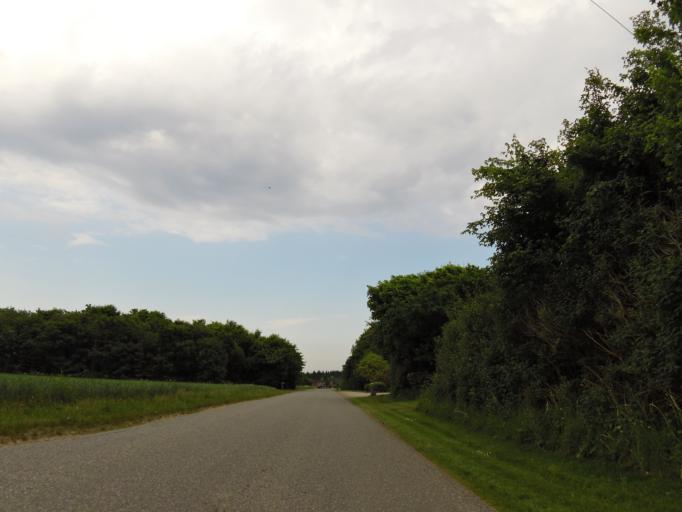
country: DK
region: Central Jutland
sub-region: Holstebro Kommune
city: Vinderup
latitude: 56.4973
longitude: 8.7842
